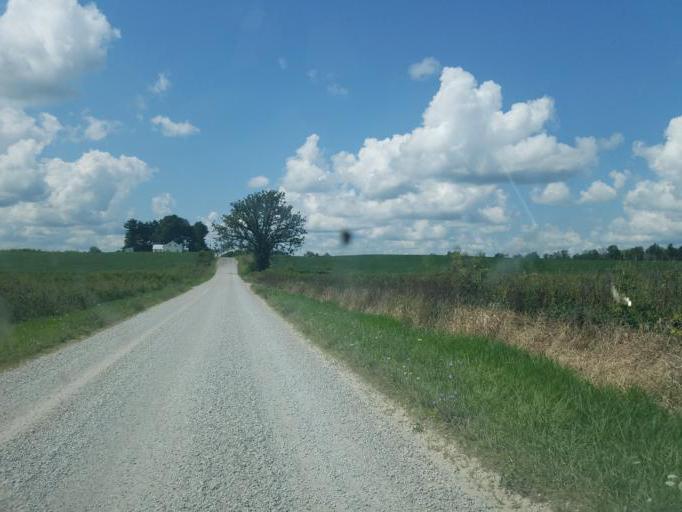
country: US
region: Ohio
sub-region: Morrow County
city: Mount Gilead
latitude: 40.5626
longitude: -82.7174
